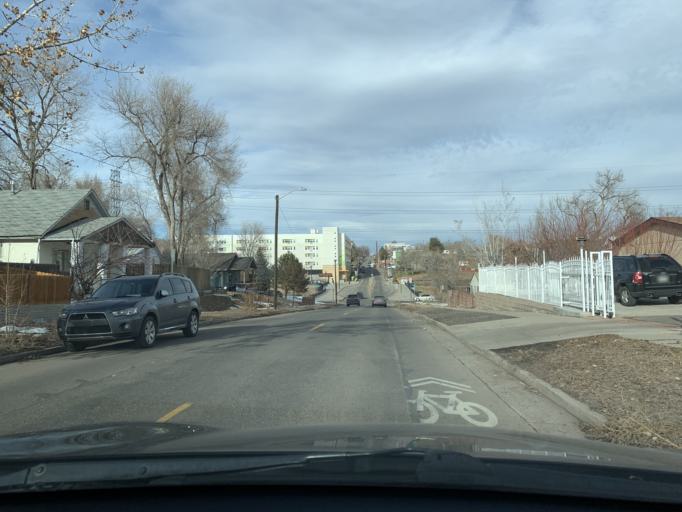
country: US
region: Colorado
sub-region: Jefferson County
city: Edgewater
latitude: 39.7338
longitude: -105.0321
